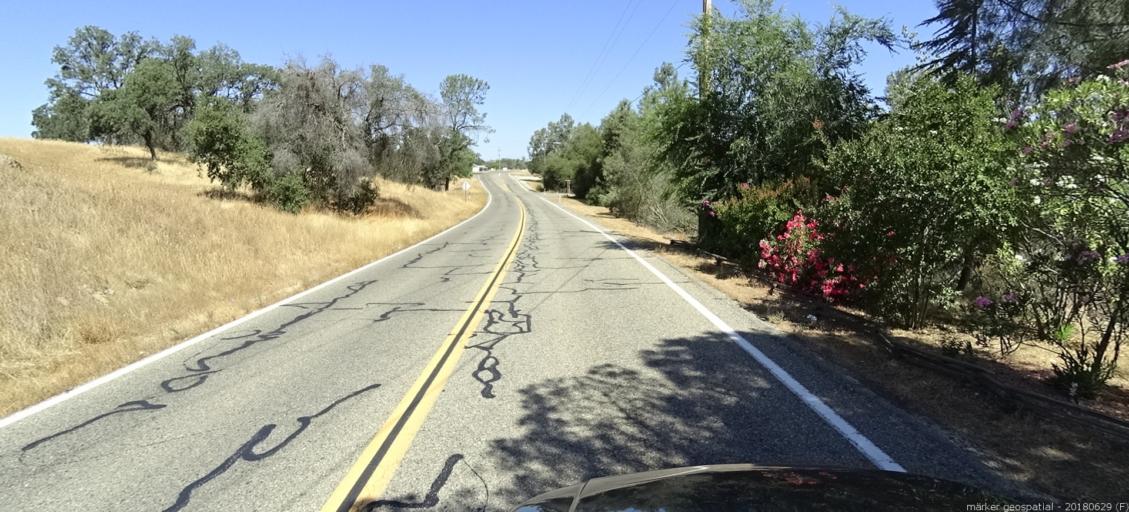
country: US
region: California
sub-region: Madera County
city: Yosemite Lakes
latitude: 37.1601
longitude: -119.7464
